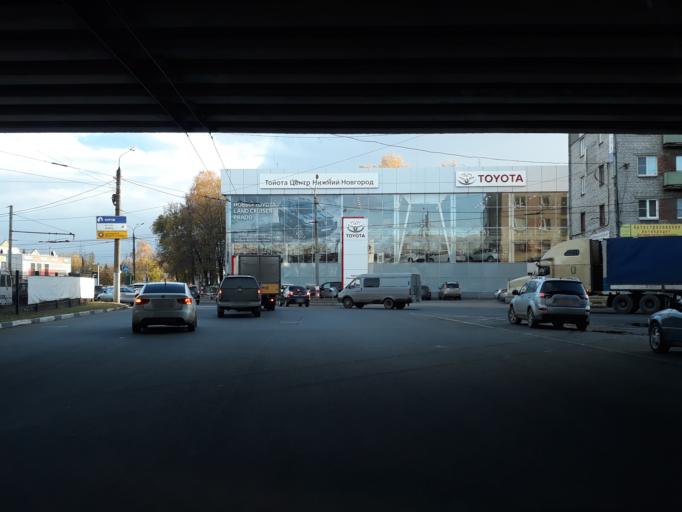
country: RU
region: Nizjnij Novgorod
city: Nizhniy Novgorod
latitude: 56.3148
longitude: 43.8981
